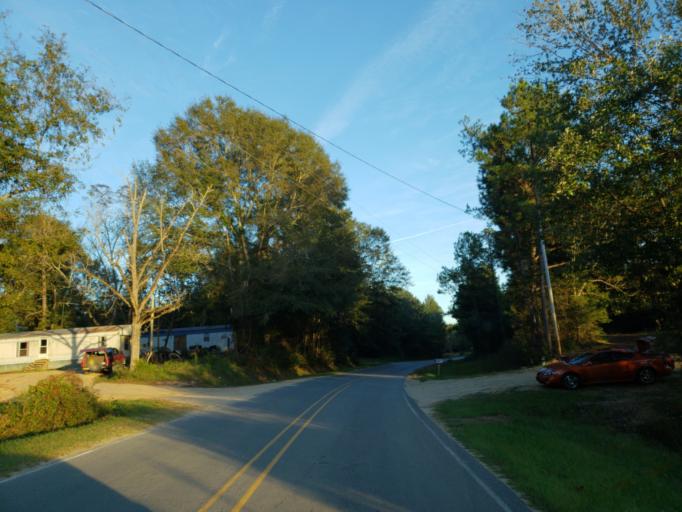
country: US
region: Mississippi
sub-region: Wayne County
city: Belmont
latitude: 31.4409
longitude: -88.5016
